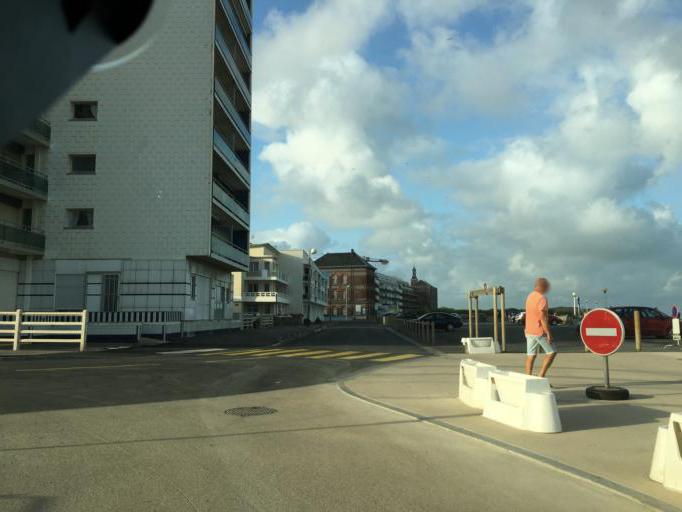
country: FR
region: Nord-Pas-de-Calais
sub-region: Departement du Pas-de-Calais
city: Berck-Plage
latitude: 50.4044
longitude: 1.5589
